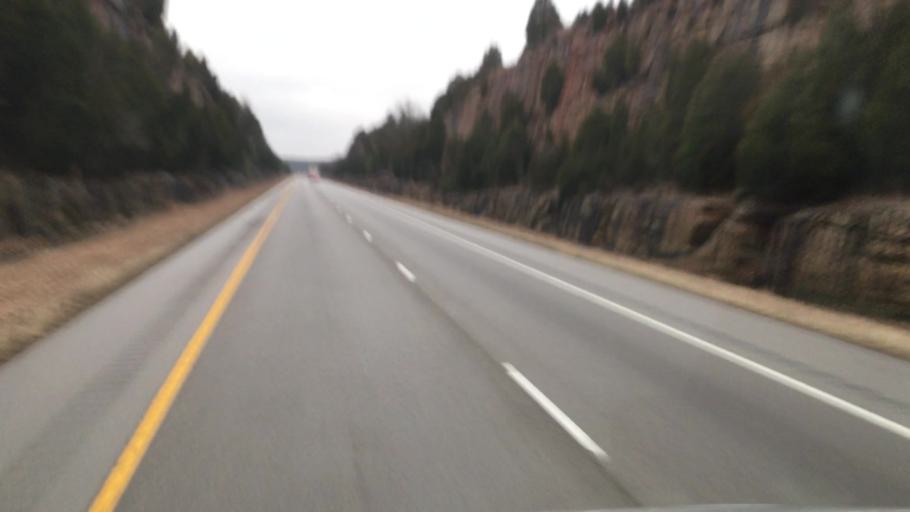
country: US
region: Illinois
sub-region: Johnson County
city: Vienna
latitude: 37.4796
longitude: -88.8922
